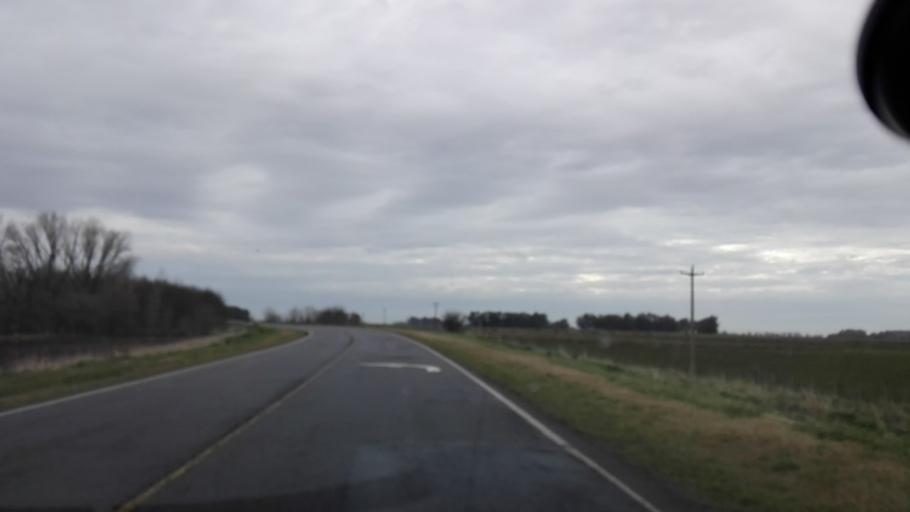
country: AR
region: Buenos Aires
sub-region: Partido de Rauch
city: Rauch
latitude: -36.6113
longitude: -59.0596
